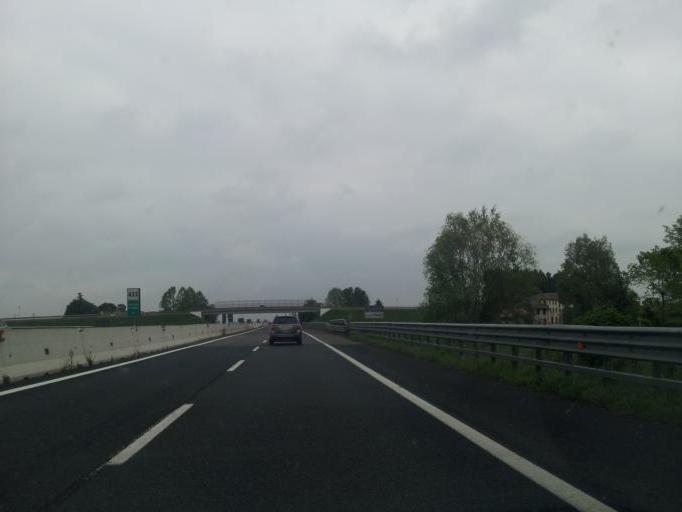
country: IT
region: Veneto
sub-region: Provincia di Treviso
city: Cessalto
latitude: 45.7106
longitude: 12.6191
